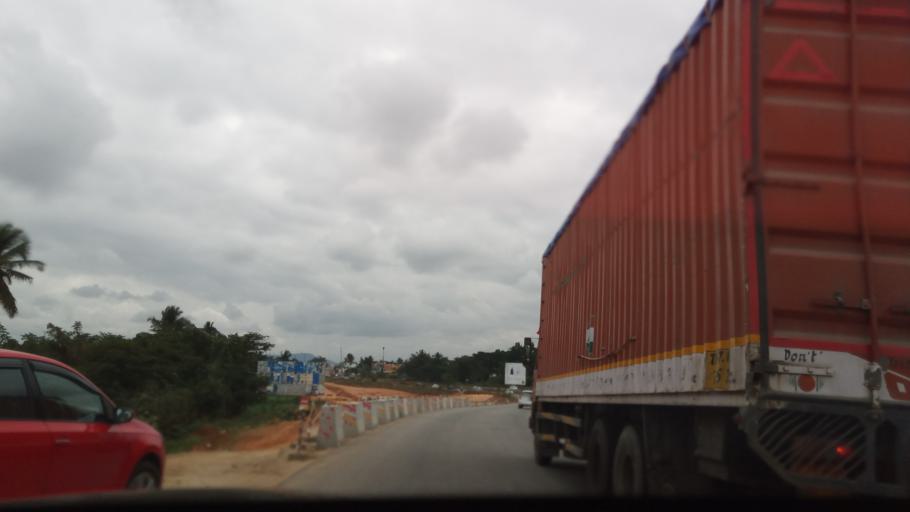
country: IN
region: Karnataka
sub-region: Mandya
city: Shrirangapattana
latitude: 12.3867
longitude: 76.6670
